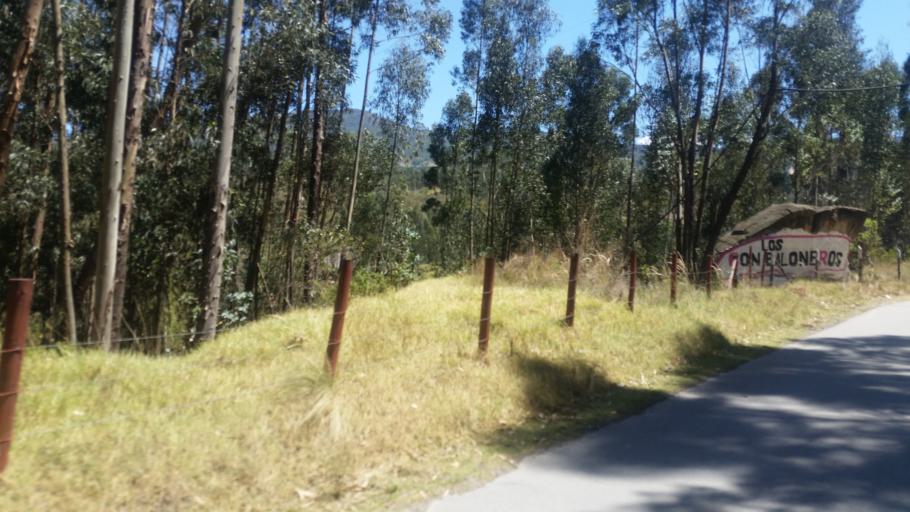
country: CO
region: Boyaca
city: Topaga
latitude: 5.7596
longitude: -72.8527
